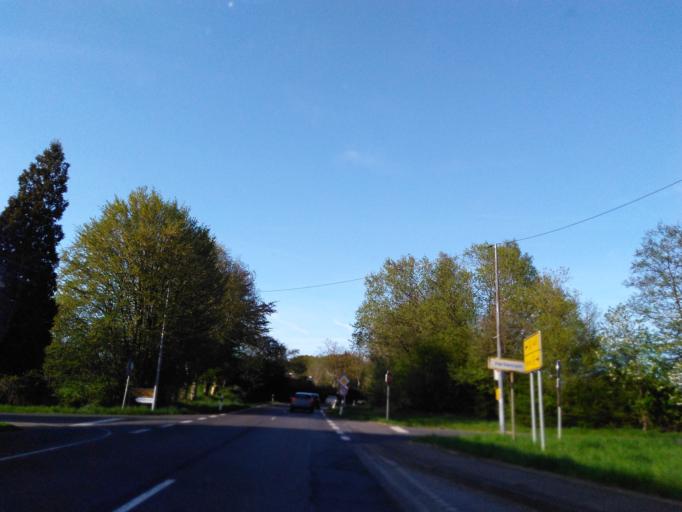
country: DE
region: North Rhine-Westphalia
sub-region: Regierungsbezirk Koln
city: Hennef
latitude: 50.8525
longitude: 7.2997
